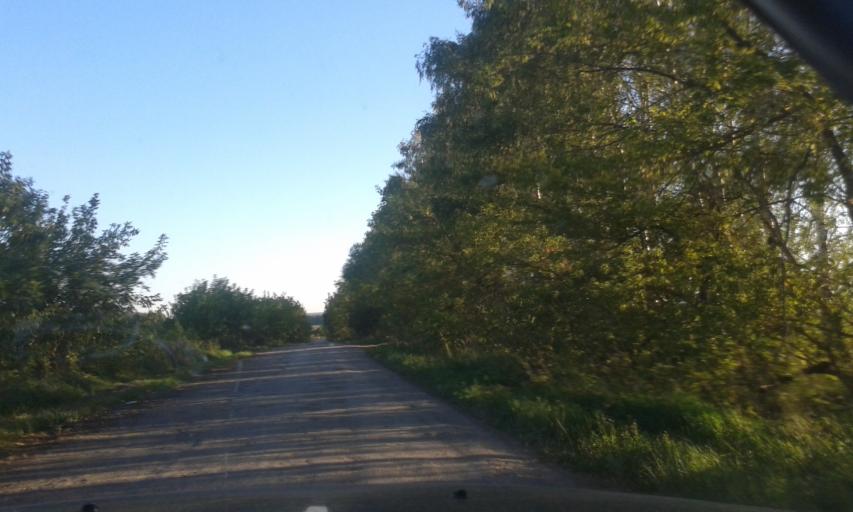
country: RU
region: Tula
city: Krapivna
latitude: 54.1280
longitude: 37.1559
